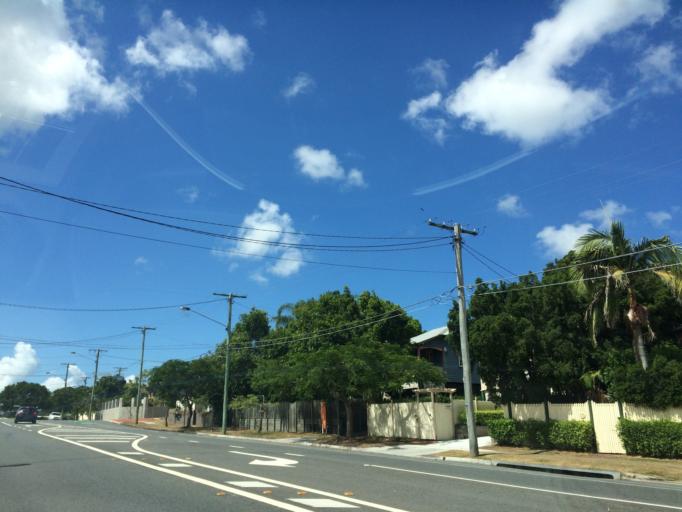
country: AU
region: Queensland
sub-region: Brisbane
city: Seven Hills
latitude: -27.4858
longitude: 153.0636
